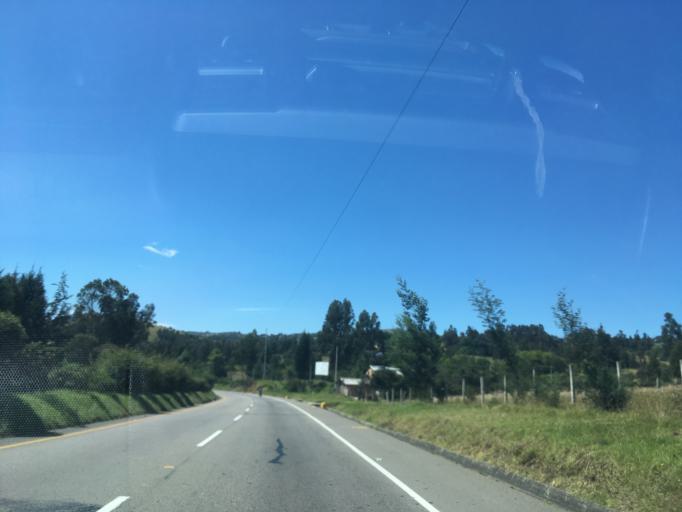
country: CO
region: Boyaca
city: Tuta
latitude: 5.6886
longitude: -73.2614
